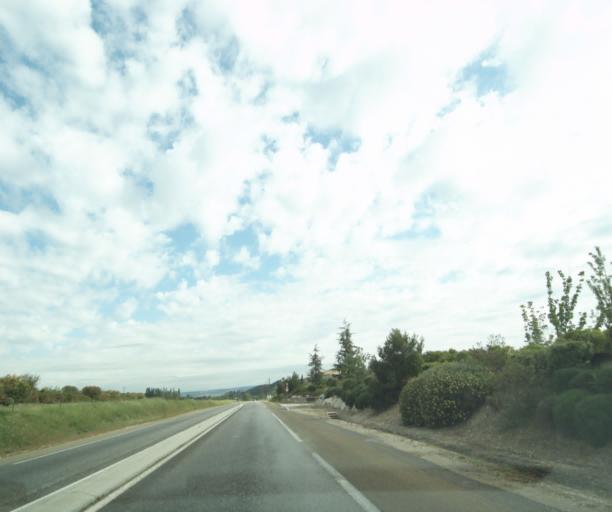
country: FR
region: Provence-Alpes-Cote d'Azur
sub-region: Departement des Bouches-du-Rhone
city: Cabries
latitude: 43.4683
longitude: 5.3543
